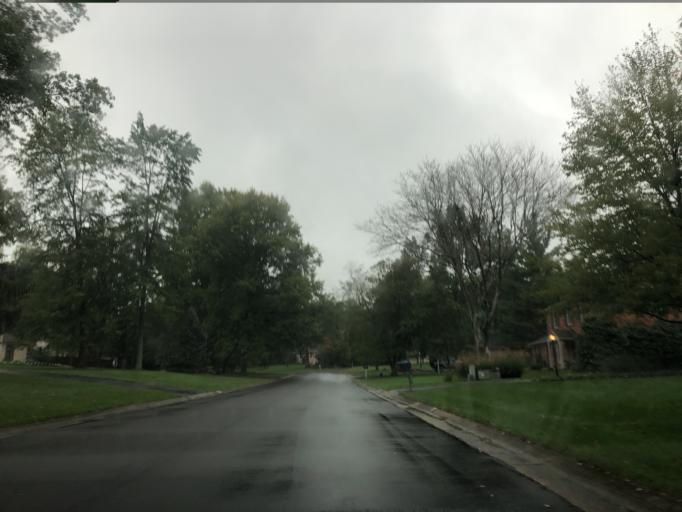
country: US
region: Ohio
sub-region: Hamilton County
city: The Village of Indian Hill
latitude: 39.2673
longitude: -84.2884
